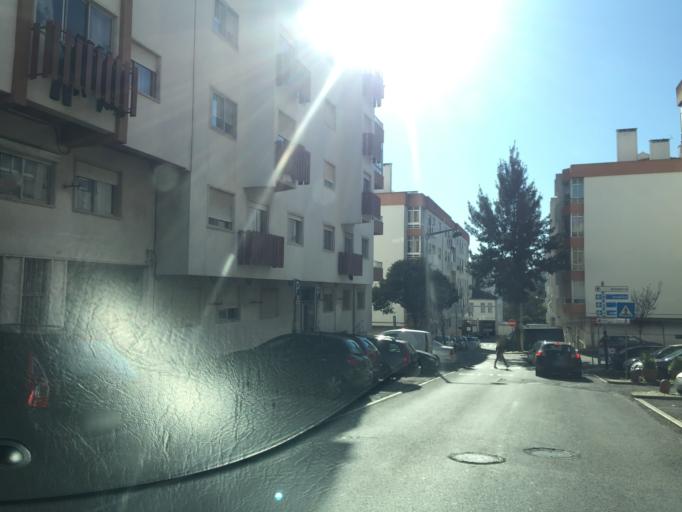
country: PT
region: Lisbon
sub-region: Sintra
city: Queluz
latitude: 38.7576
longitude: -9.2505
